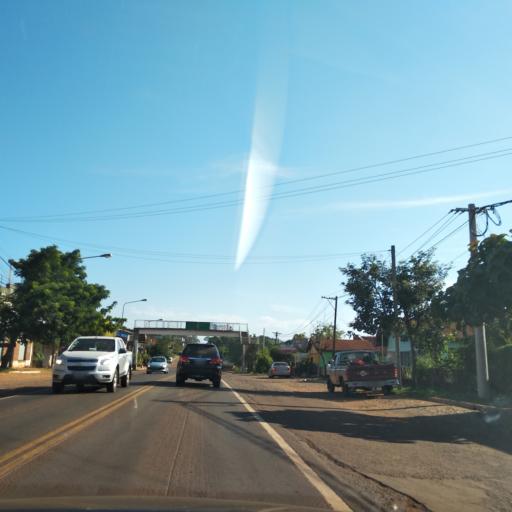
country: AR
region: Misiones
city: Gobernador Roca
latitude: -27.1854
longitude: -55.4636
